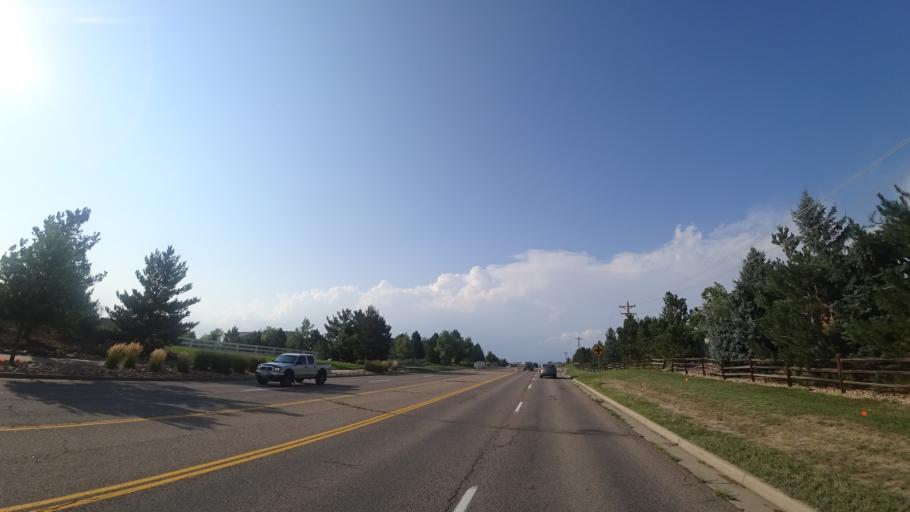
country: US
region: Colorado
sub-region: Douglas County
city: Parker
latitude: 39.5986
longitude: -104.7448
